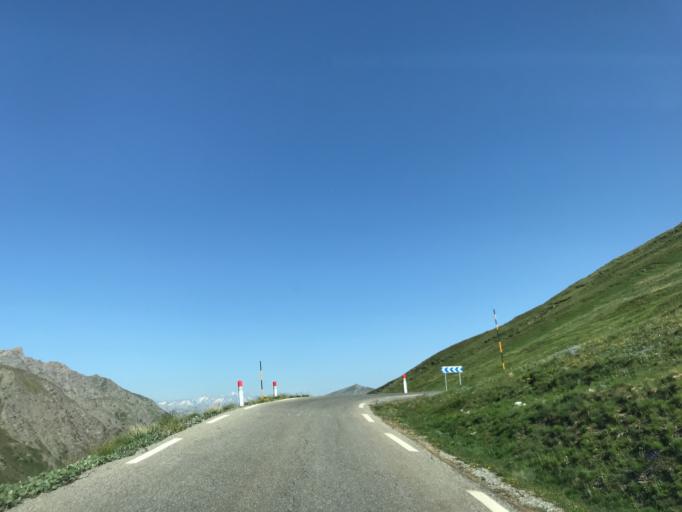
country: IT
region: Piedmont
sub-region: Provincia di Cuneo
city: Pontechianale
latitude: 44.6927
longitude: 6.9650
